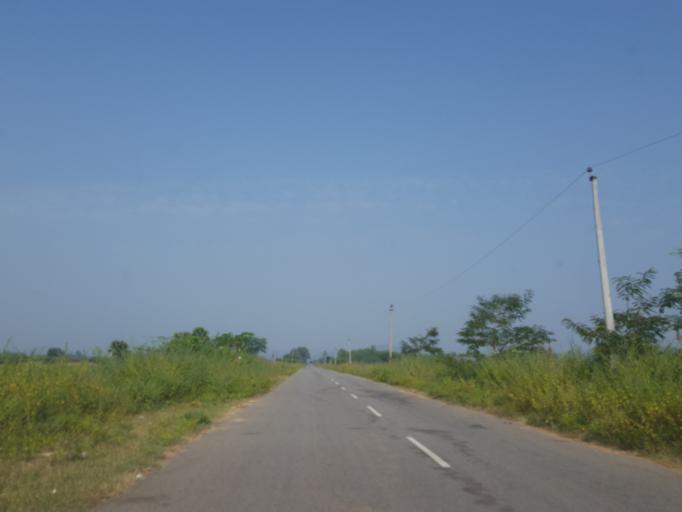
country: IN
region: Telangana
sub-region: Khammam
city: Yellandu
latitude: 17.6441
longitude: 80.2960
